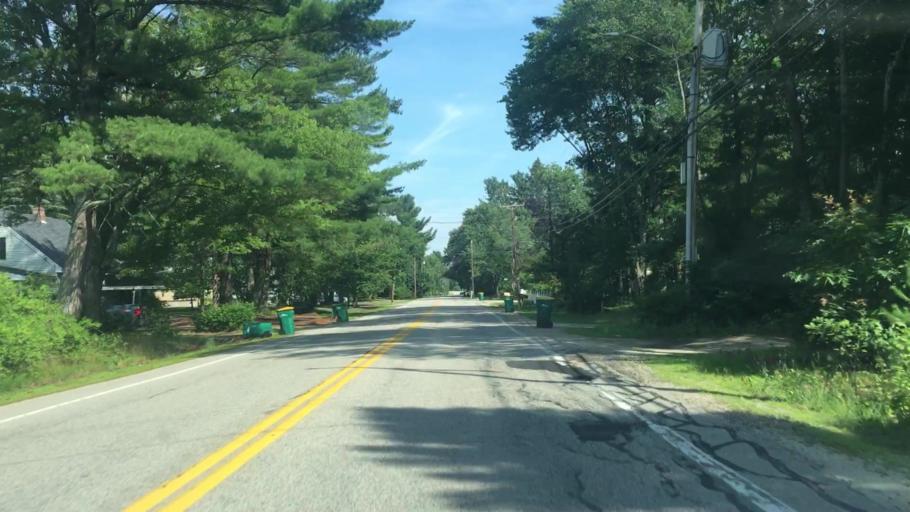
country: US
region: New Hampshire
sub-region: Strafford County
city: Rochester
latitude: 43.2796
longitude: -70.9680
